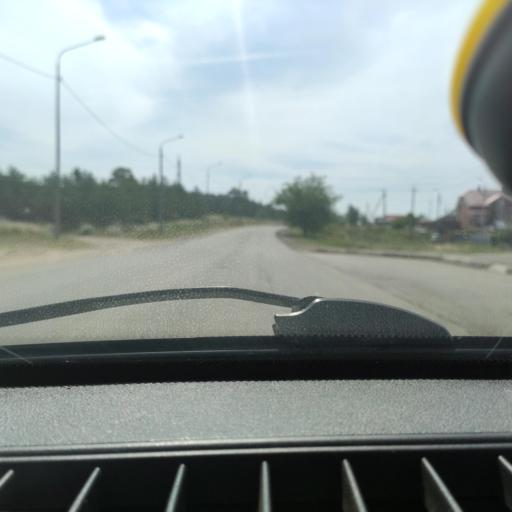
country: RU
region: Samara
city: Zhigulevsk
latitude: 53.4880
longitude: 49.5356
